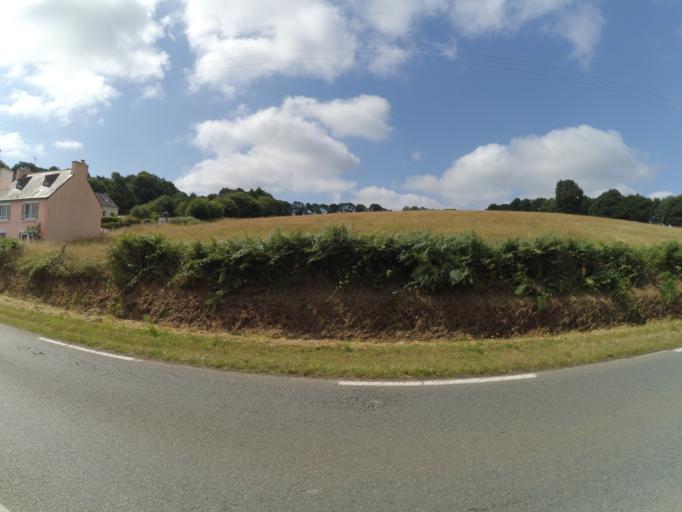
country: FR
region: Brittany
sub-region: Departement du Finistere
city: Rosporden
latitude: 47.9555
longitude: -3.8141
